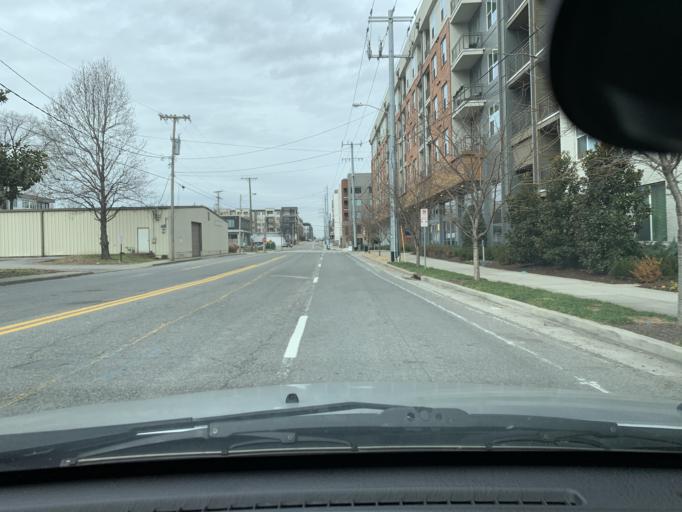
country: US
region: Tennessee
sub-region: Davidson County
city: Nashville
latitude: 36.1754
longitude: -86.7849
